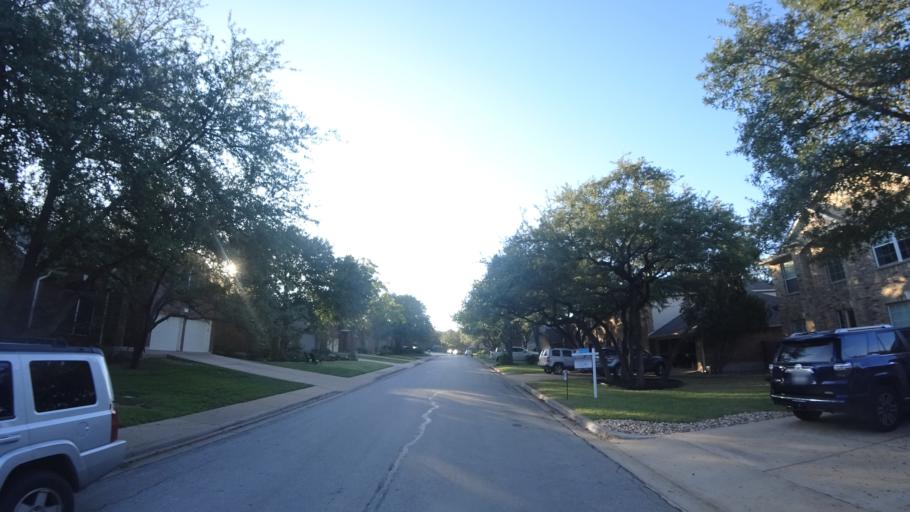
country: US
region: Texas
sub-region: Travis County
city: Hudson Bend
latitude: 30.3810
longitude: -97.8948
